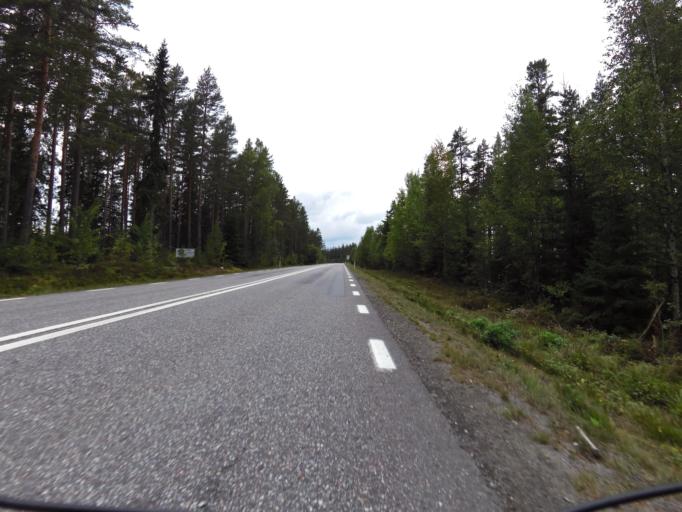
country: SE
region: Gaevleborg
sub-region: Ockelbo Kommun
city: Ockelbo
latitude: 60.8843
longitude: 16.8116
